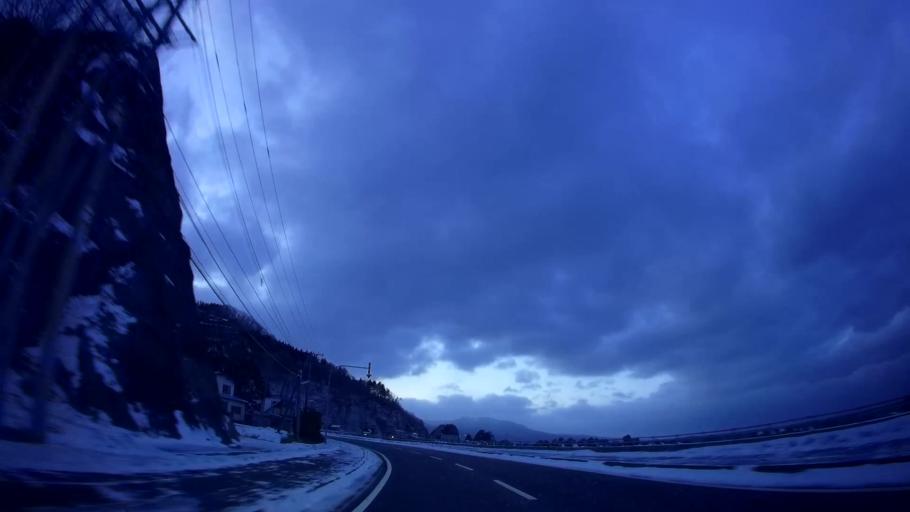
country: JP
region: Hokkaido
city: Hakodate
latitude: 41.8897
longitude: 141.0595
